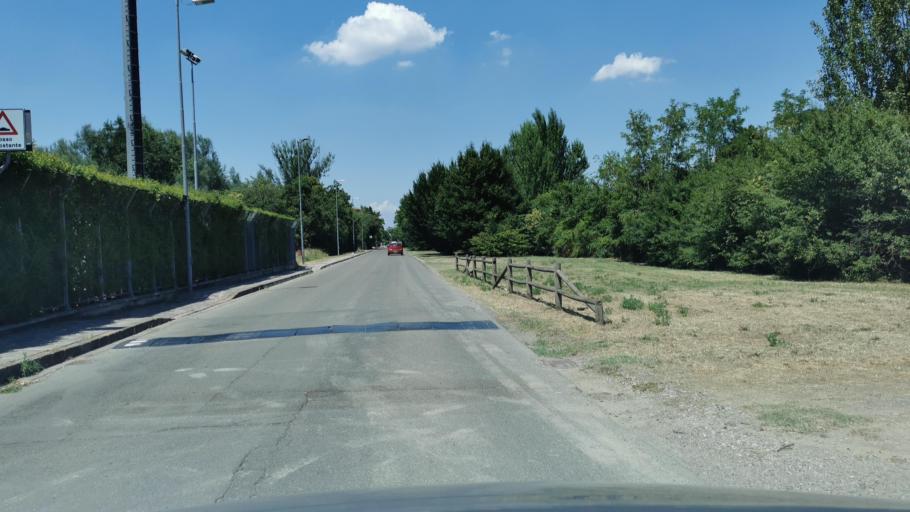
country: IT
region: Emilia-Romagna
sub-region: Provincia di Modena
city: Carpi Centro
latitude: 44.7970
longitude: 10.8884
